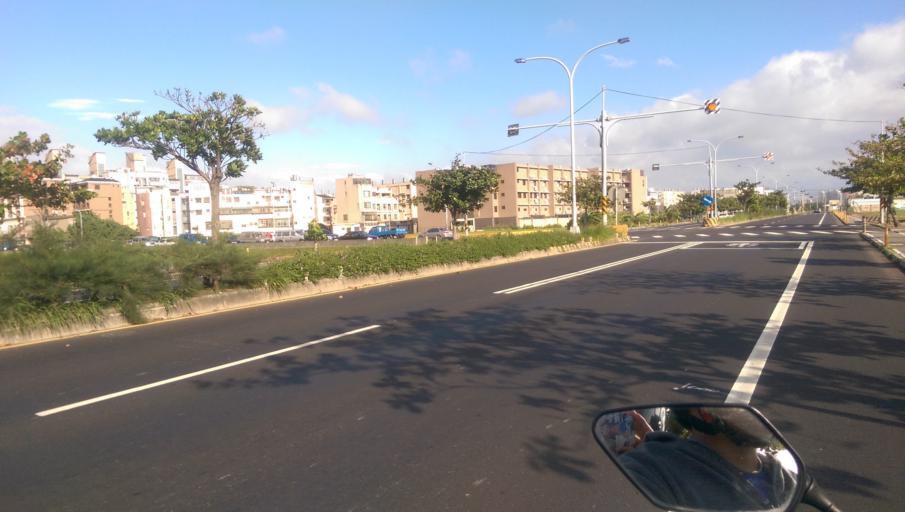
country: TW
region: Taiwan
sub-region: Hsinchu
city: Hsinchu
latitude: 24.8358
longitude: 120.9402
